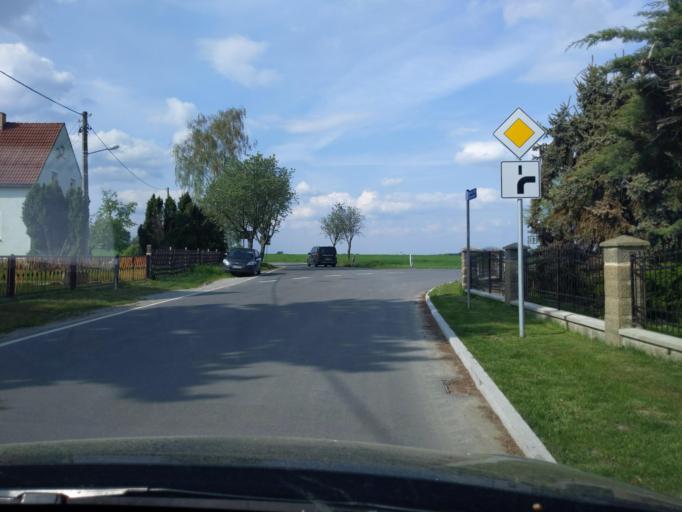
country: DE
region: Saxony
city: Malschwitz
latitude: 51.2143
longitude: 14.5293
